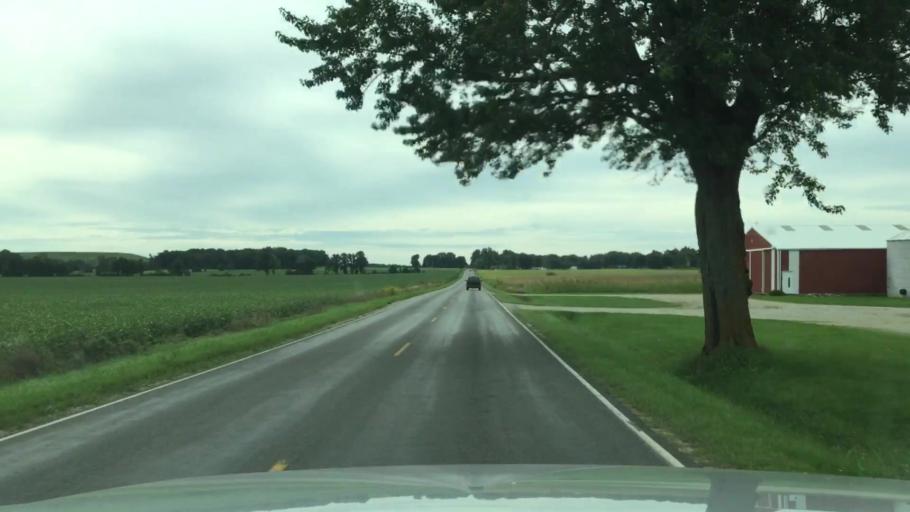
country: US
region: Michigan
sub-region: Shiawassee County
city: Durand
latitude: 42.9945
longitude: -83.9868
